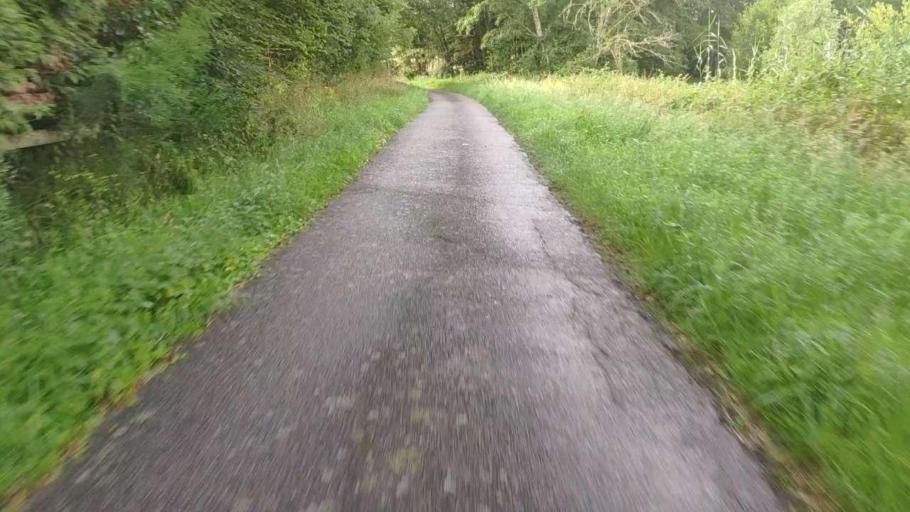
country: FR
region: Franche-Comte
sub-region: Departement du Jura
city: Bletterans
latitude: 46.8641
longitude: 5.5259
